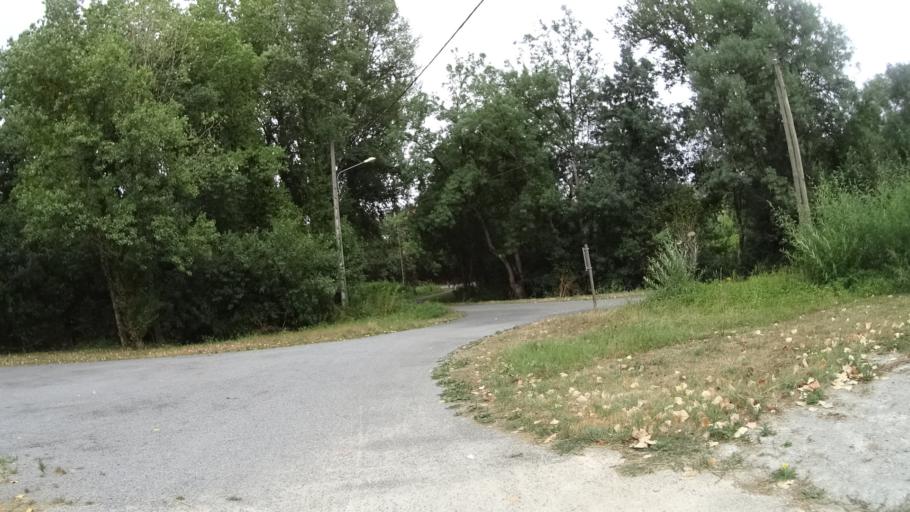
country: FR
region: Pays de la Loire
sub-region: Departement de la Loire-Atlantique
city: Saint-Jean-de-Boiseau
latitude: 47.1993
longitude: -1.7256
